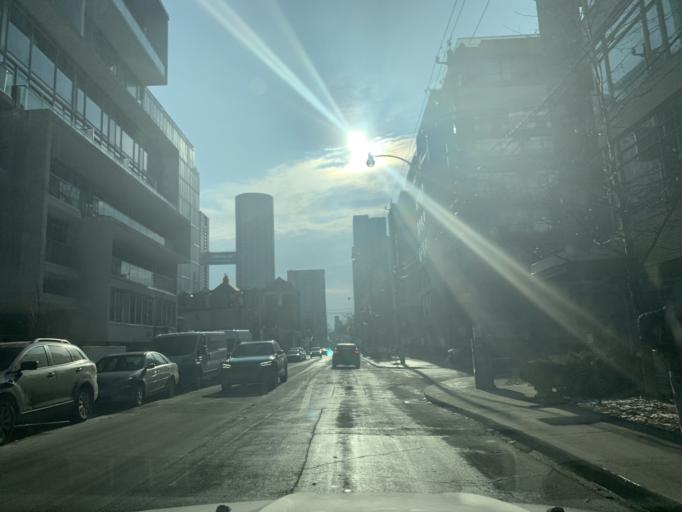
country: CA
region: Ontario
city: Toronto
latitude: 43.6439
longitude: -79.3999
